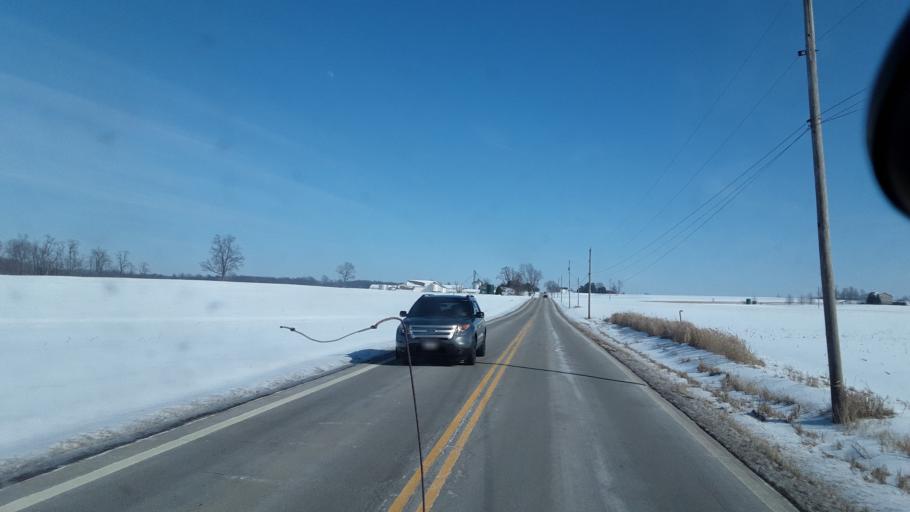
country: US
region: Ohio
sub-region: Mahoning County
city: Sebring
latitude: 40.9449
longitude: -80.9341
